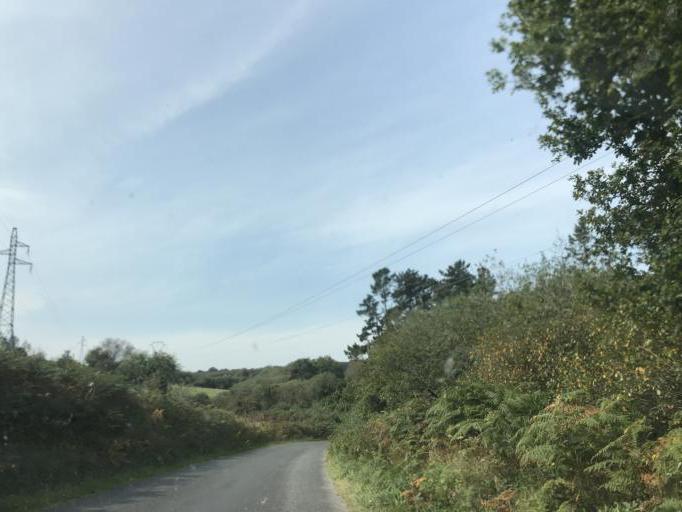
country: FR
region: Brittany
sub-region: Departement du Finistere
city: Brasparts
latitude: 48.3346
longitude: -3.9026
